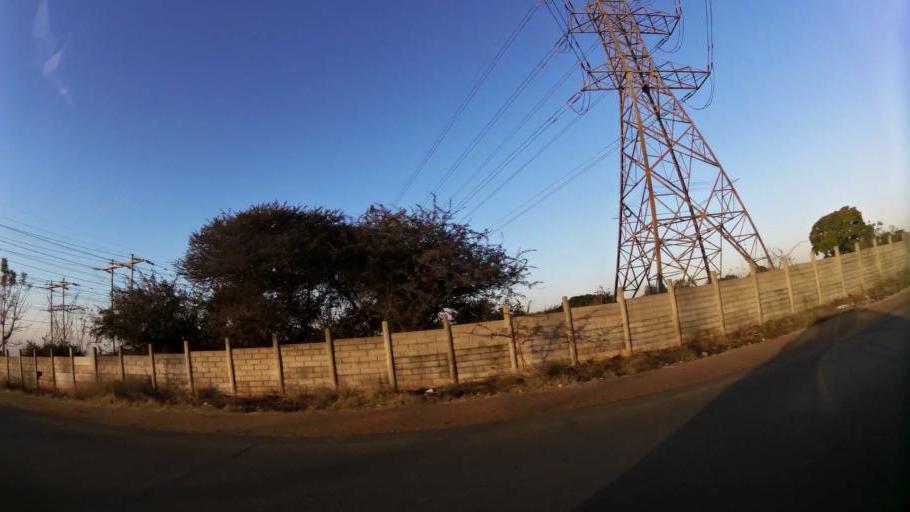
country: ZA
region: North-West
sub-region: Bojanala Platinum District Municipality
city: Rustenburg
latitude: -25.6318
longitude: 27.2023
